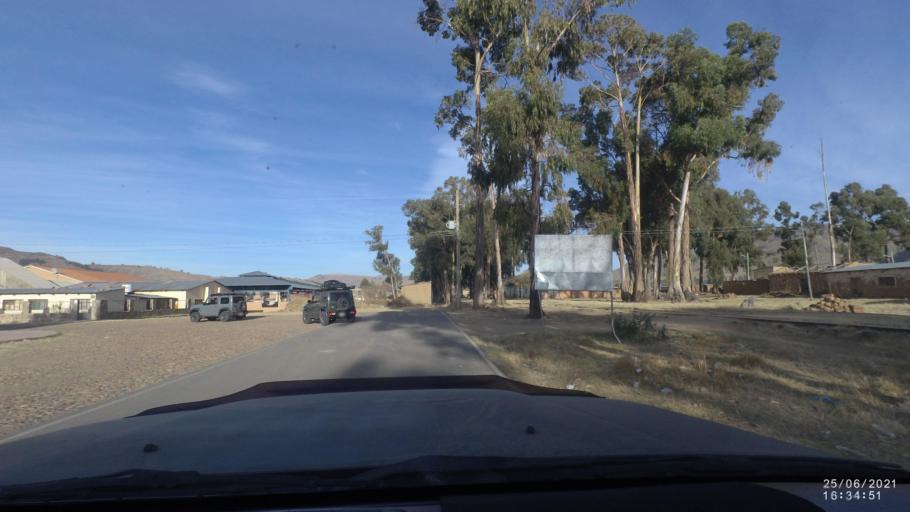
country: BO
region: Cochabamba
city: Arani
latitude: -17.8177
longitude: -65.7787
